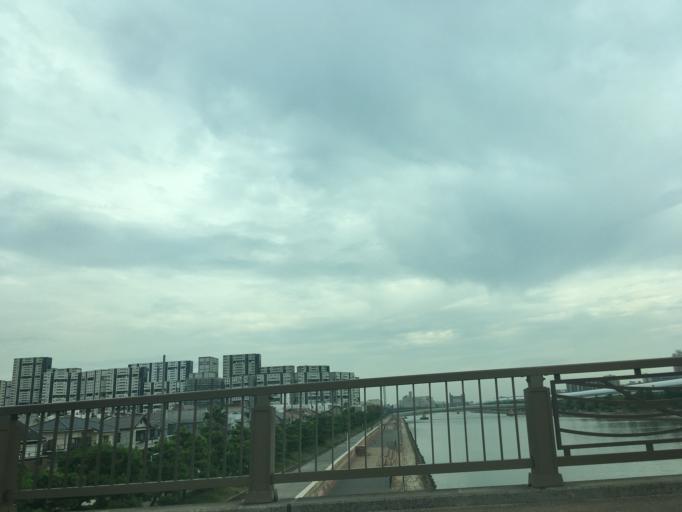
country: JP
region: Hyogo
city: Ashiya
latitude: 34.7152
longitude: 135.3088
